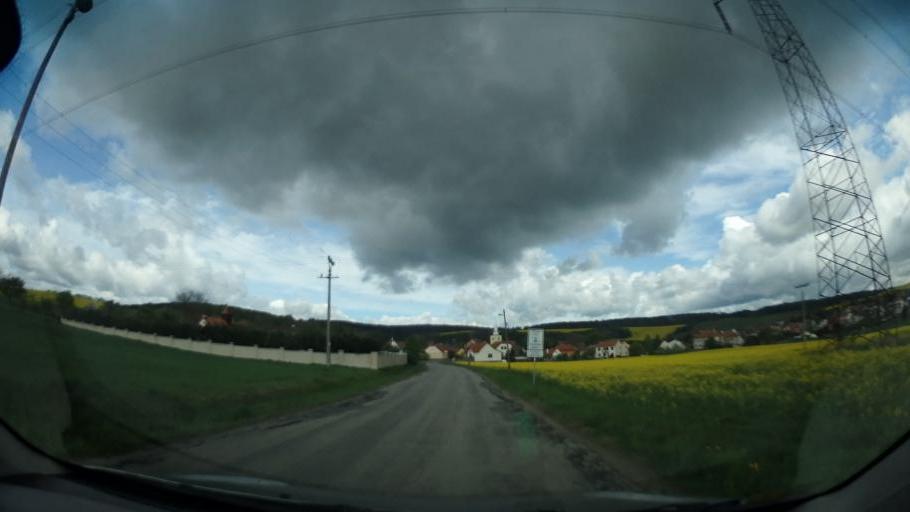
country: CZ
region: South Moravian
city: Ricany
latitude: 49.2327
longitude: 16.4082
